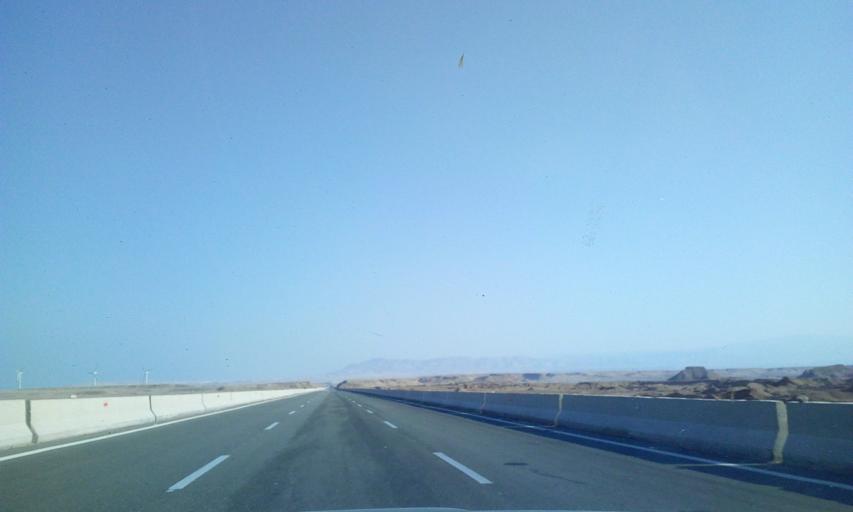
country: EG
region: As Suways
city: Ain Sukhna
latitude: 29.1737
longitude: 32.5057
